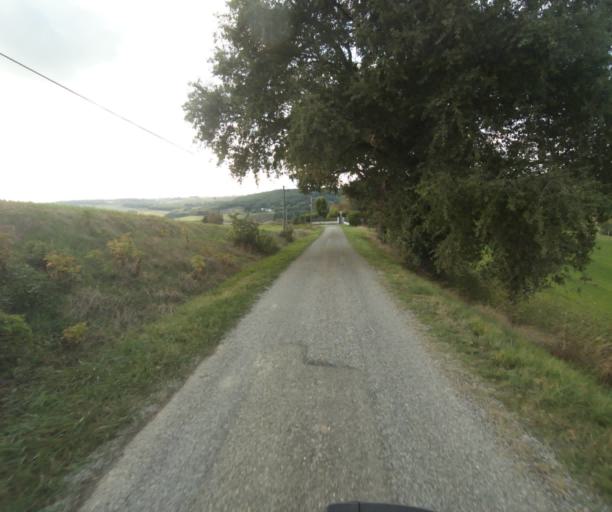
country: FR
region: Midi-Pyrenees
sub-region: Departement de la Haute-Garonne
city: Launac
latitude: 43.8071
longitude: 1.1219
